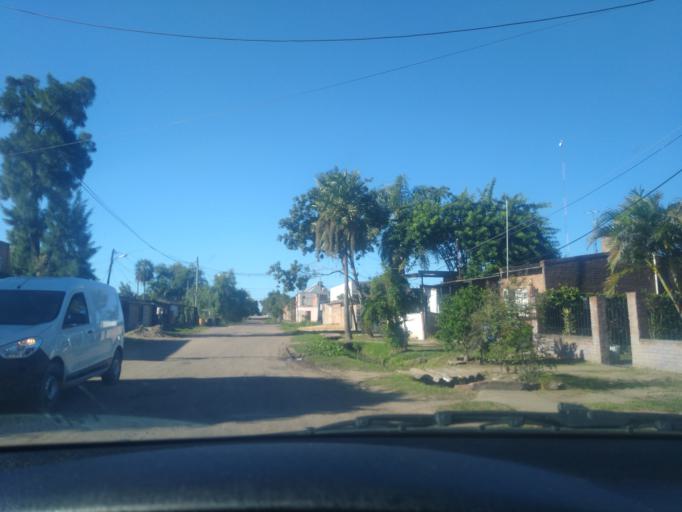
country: AR
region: Chaco
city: Puerto Vilelas
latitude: -27.5155
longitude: -58.9440
